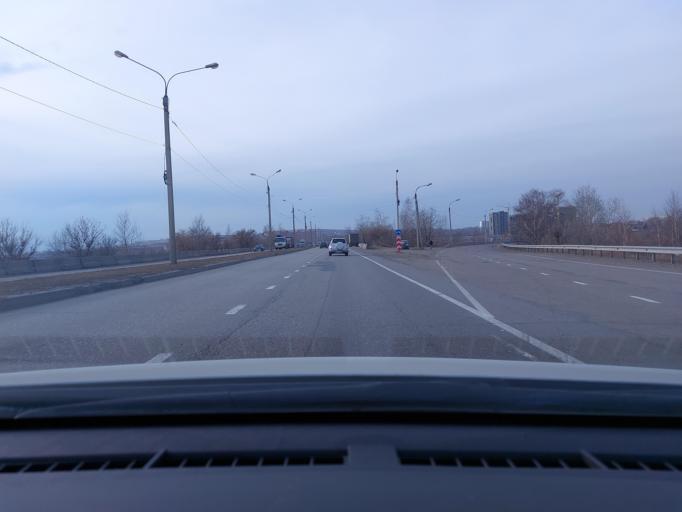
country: RU
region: Irkutsk
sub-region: Irkutskiy Rayon
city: Irkutsk
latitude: 52.3251
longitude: 104.2208
